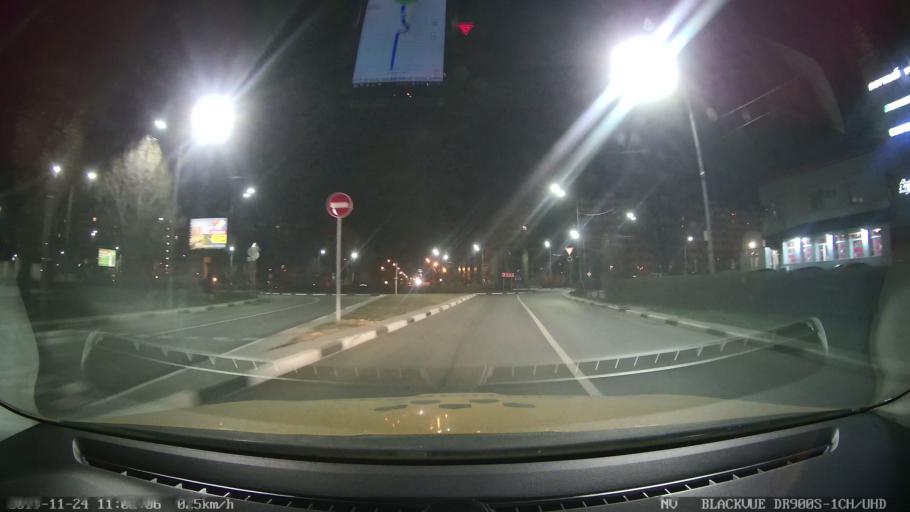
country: RU
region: Moskovskaya
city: Mytishchi
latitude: 55.9062
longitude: 37.7072
